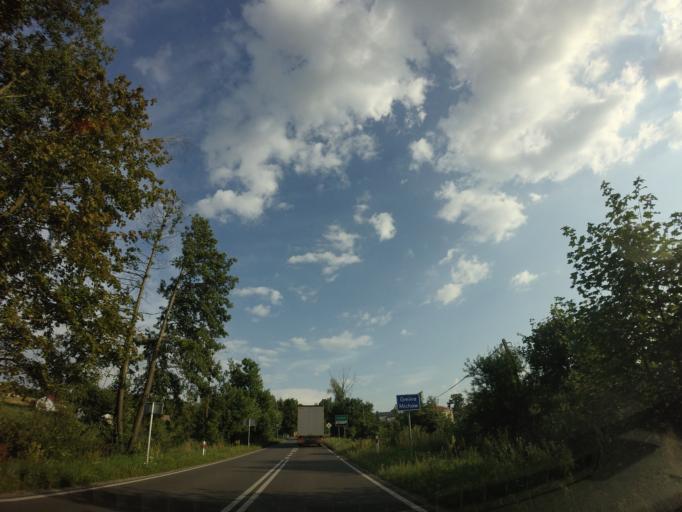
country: PL
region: Lublin Voivodeship
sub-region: Powiat lubartowski
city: Jeziorzany
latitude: 51.5905
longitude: 22.2827
